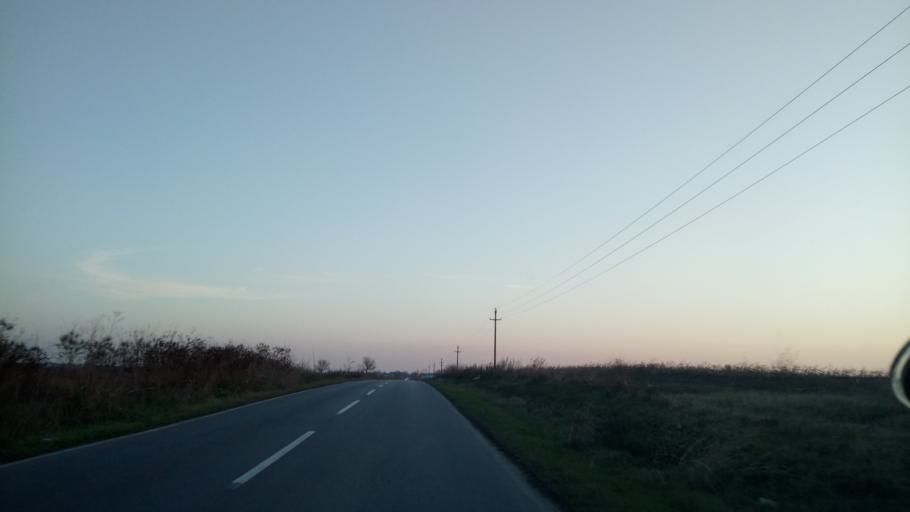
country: RS
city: Belegis
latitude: 45.0398
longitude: 20.3333
